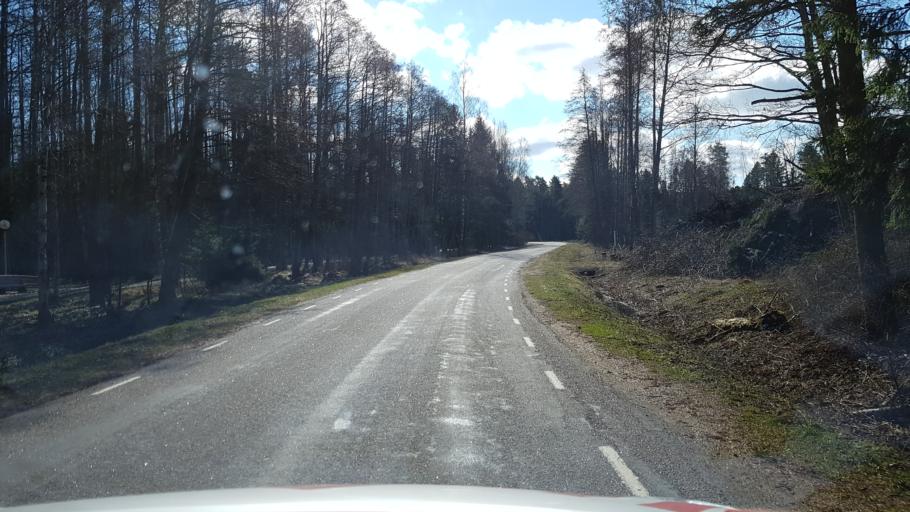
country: EE
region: Harju
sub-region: Loksa linn
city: Loksa
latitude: 59.5801
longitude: 25.9172
